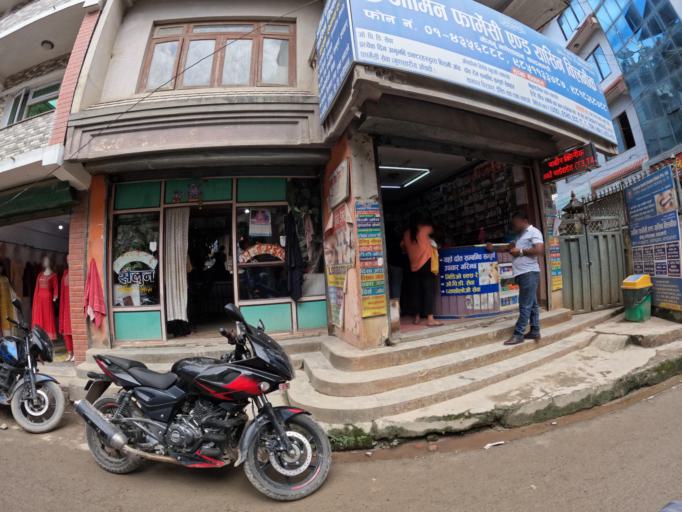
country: NP
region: Central Region
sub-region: Bagmati Zone
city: Kathmandu
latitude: 27.7417
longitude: 85.3149
